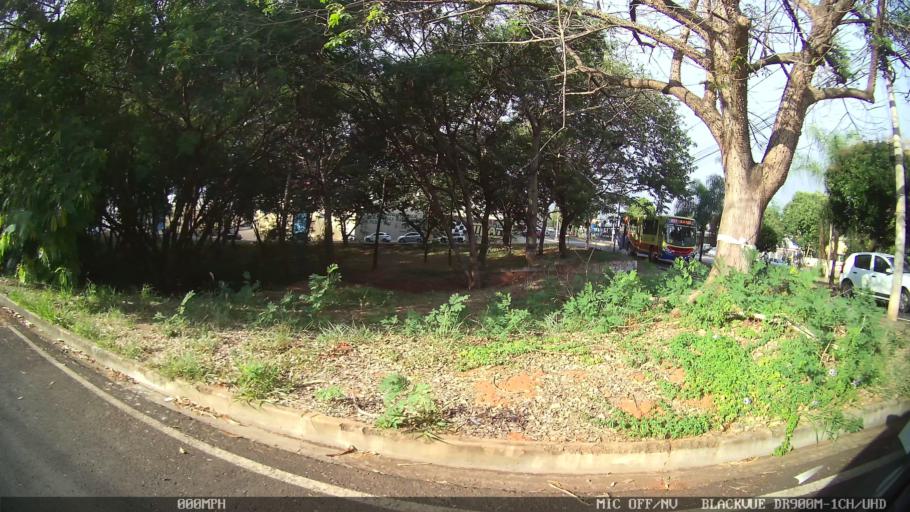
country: BR
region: Sao Paulo
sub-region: Sao Jose Do Rio Preto
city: Sao Jose do Rio Preto
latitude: -20.8370
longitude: -49.3710
